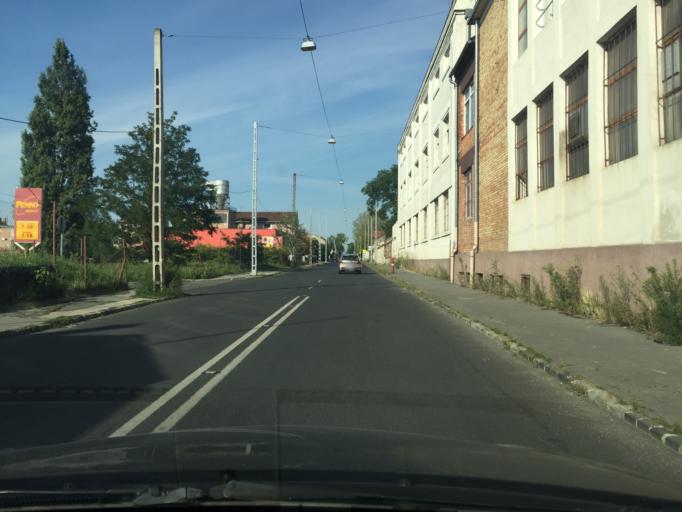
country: HU
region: Budapest
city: Budapest IV. keruelet
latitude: 47.5652
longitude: 19.0807
